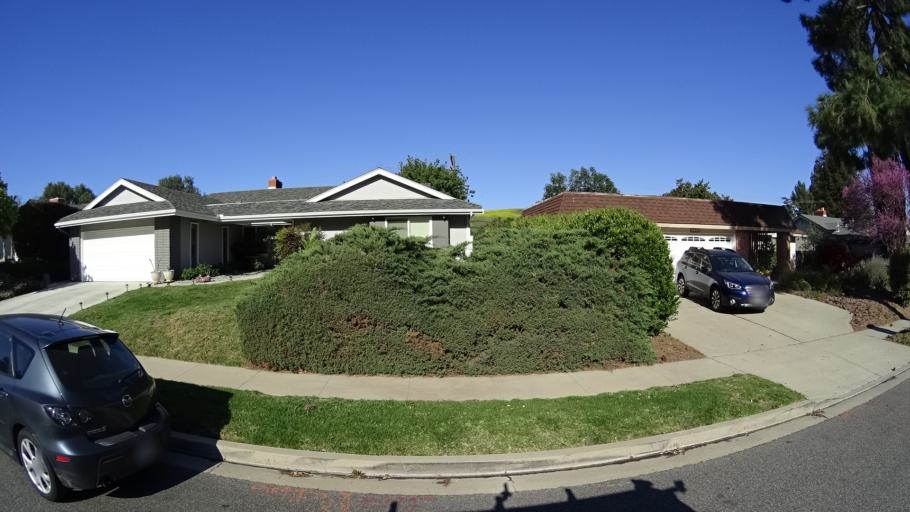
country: US
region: California
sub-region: Ventura County
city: Thousand Oaks
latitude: 34.1982
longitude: -118.8418
